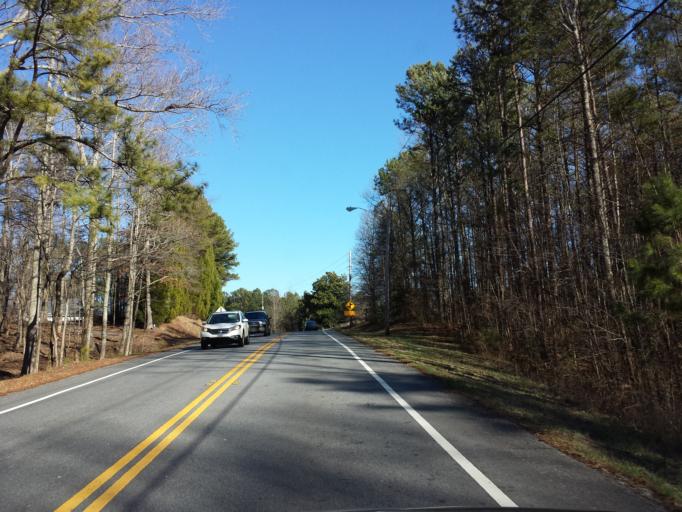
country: US
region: Georgia
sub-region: Cobb County
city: Kennesaw
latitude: 33.9651
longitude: -84.6569
